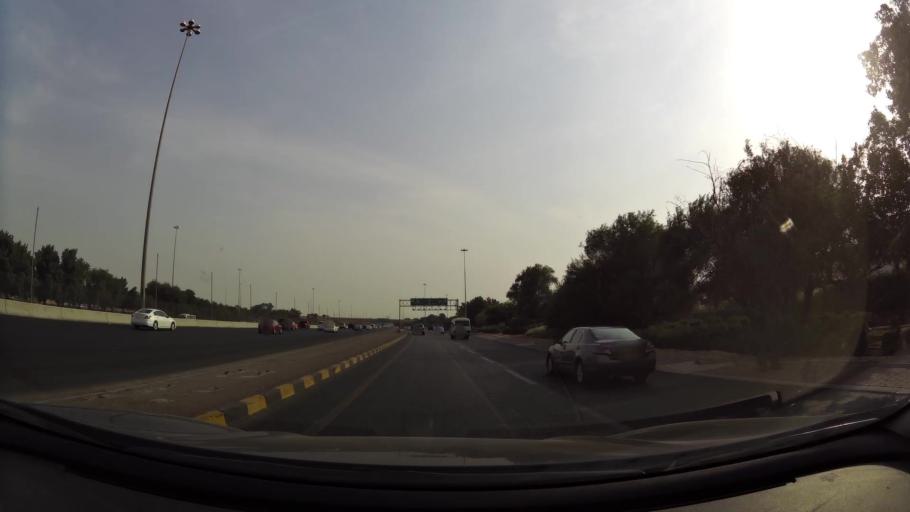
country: KW
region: Al Farwaniyah
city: Janub as Surrah
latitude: 29.2716
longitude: 47.9868
